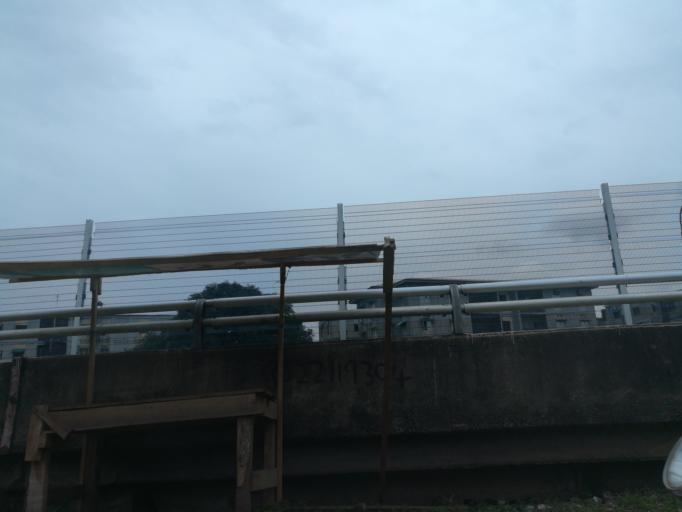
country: NG
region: Lagos
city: Makoko
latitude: 6.4927
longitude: 3.3861
